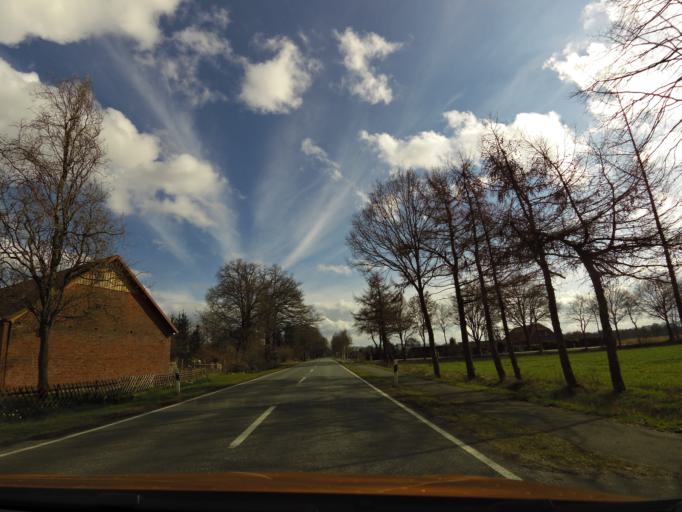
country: DE
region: Lower Saxony
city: Oldenburg
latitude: 53.0986
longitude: 8.2837
